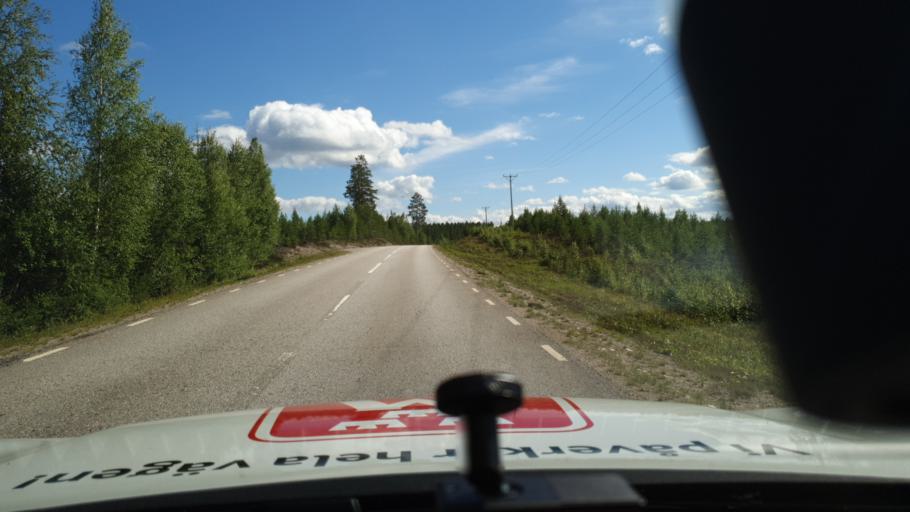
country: NO
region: Hedmark
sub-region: Trysil
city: Innbygda
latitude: 60.9927
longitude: 12.4920
